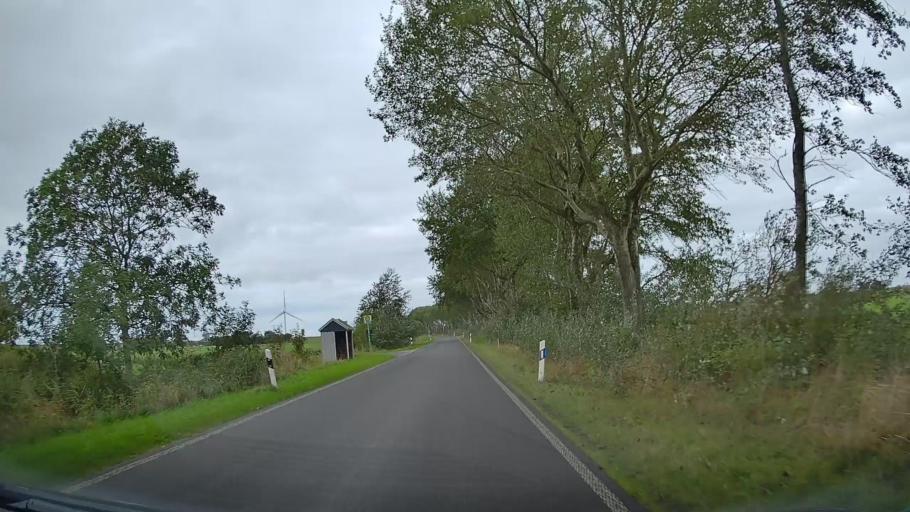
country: DE
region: Schleswig-Holstein
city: Friedrich-Wilhelm-Lubke-Koog
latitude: 54.8361
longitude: 8.6560
